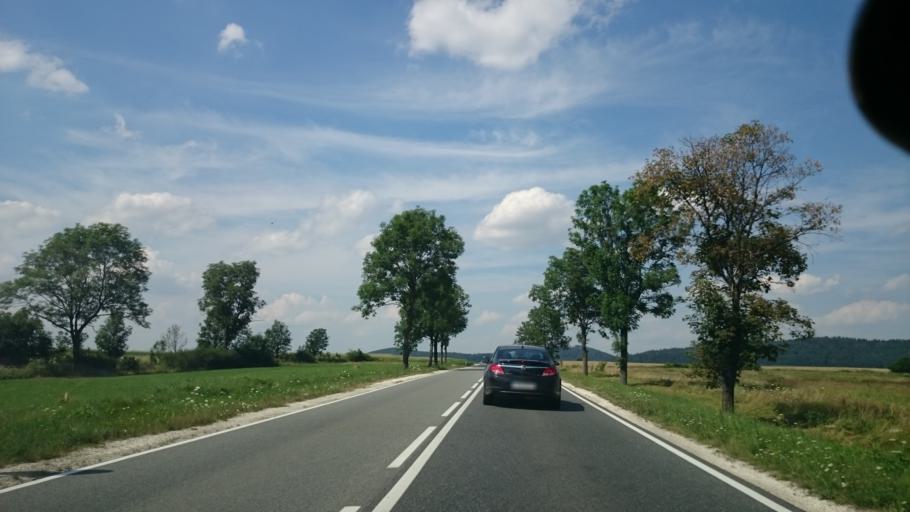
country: PL
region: Lower Silesian Voivodeship
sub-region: Powiat klodzki
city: Bystrzyca Klodzka
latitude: 50.3260
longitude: 16.6617
